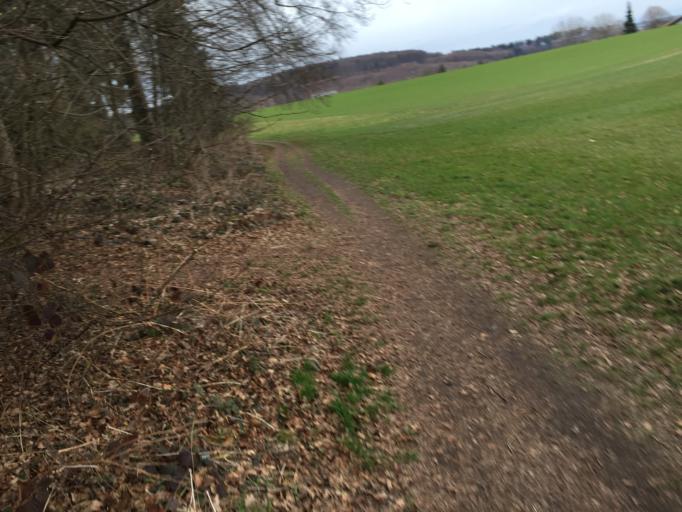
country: CH
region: Bern
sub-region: Bern-Mittelland District
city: Koniz
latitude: 46.9150
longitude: 7.4123
